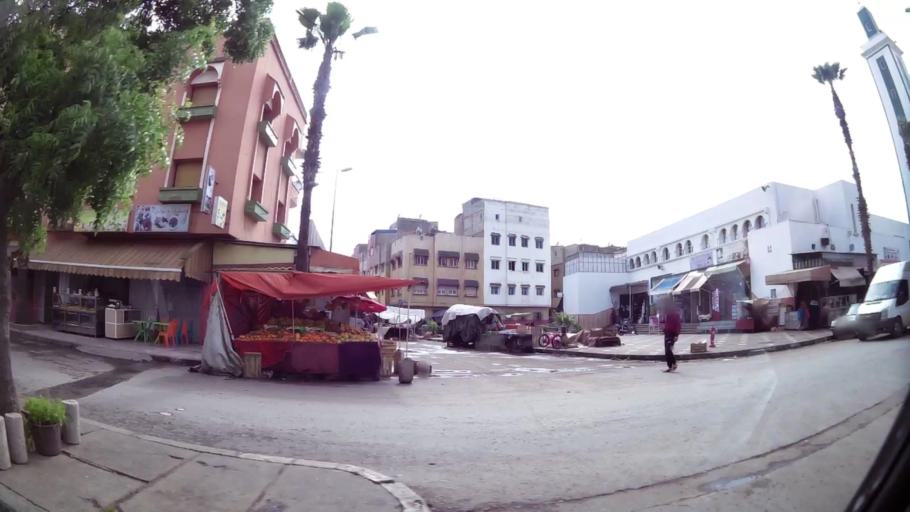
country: MA
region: Grand Casablanca
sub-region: Mohammedia
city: Mohammedia
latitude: 33.6814
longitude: -7.3765
